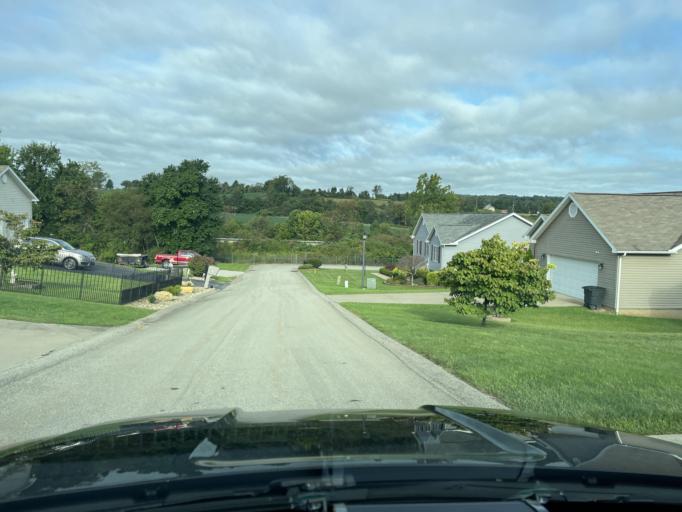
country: US
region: Pennsylvania
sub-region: Fayette County
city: Leith-Hatfield
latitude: 39.8784
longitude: -79.7429
